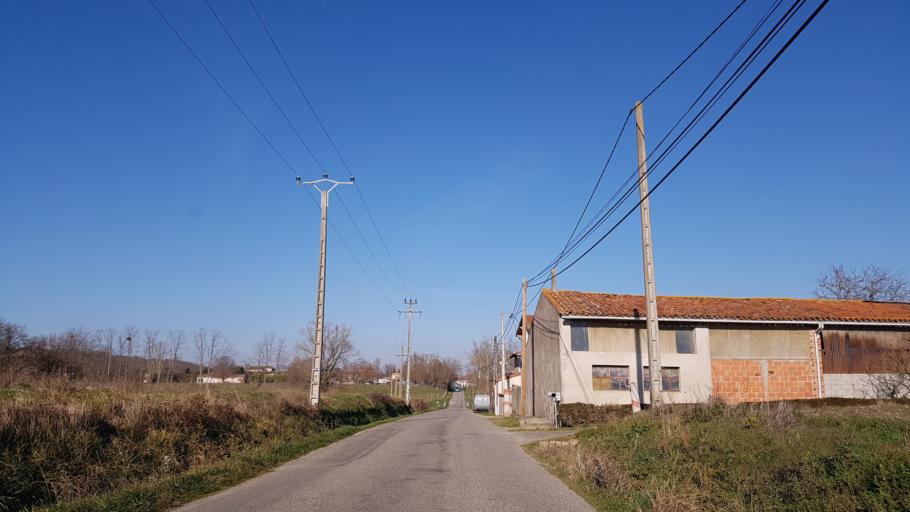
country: FR
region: Midi-Pyrenees
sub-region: Departement de l'Ariege
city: La Tour-du-Crieu
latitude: 43.1035
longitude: 1.7230
